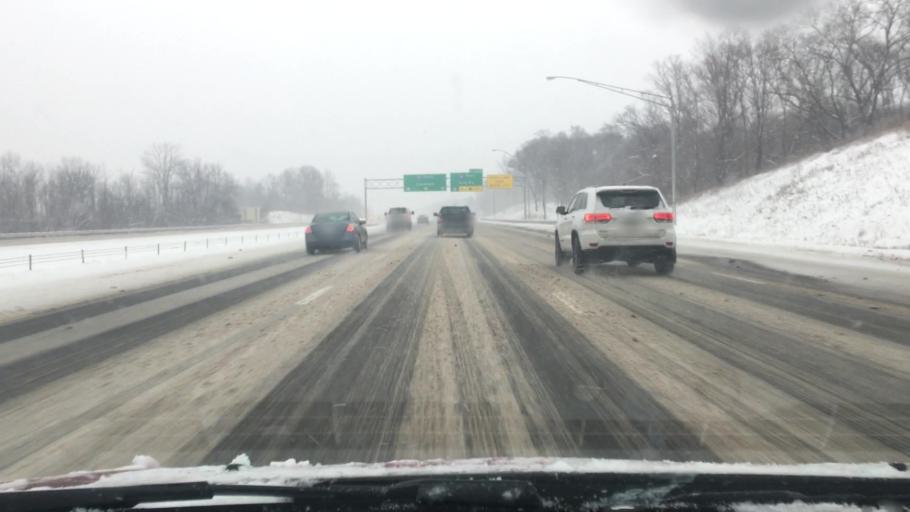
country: US
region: Ohio
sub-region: Medina County
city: Medina
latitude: 41.1461
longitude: -81.7900
